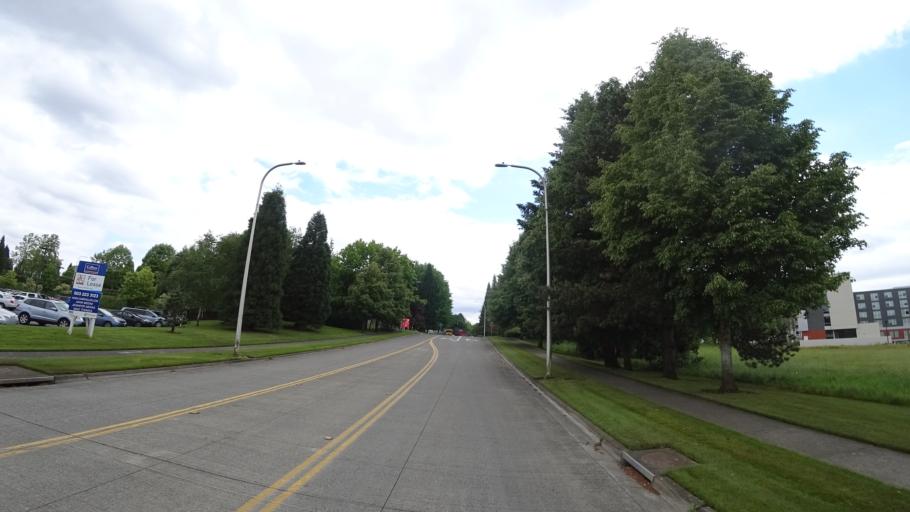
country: US
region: Oregon
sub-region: Washington County
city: Rockcreek
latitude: 45.5338
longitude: -122.8821
